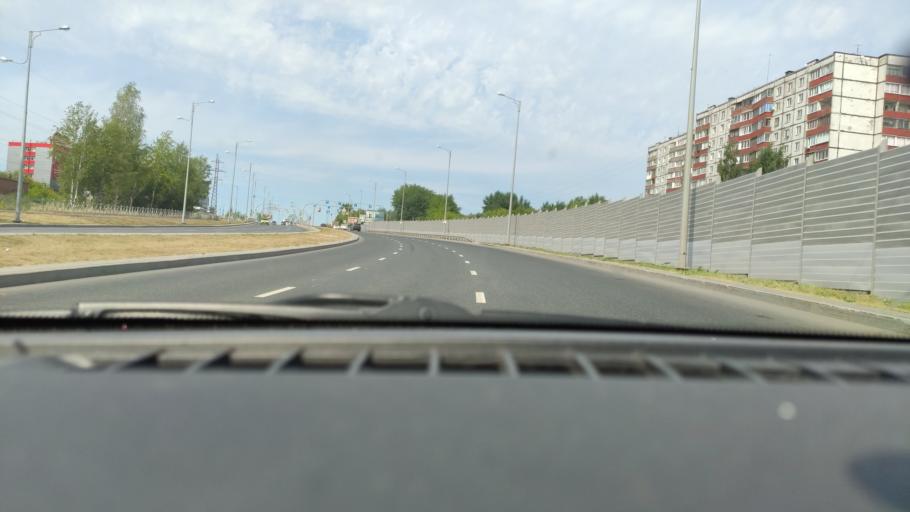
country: RU
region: Perm
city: Froly
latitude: 57.9456
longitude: 56.2686
